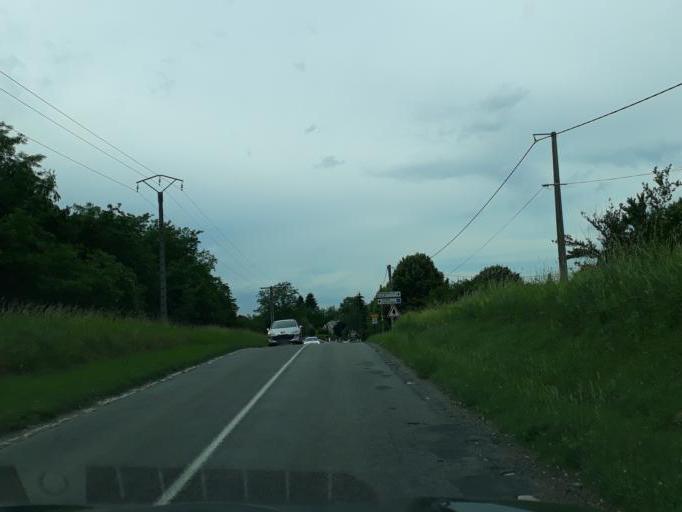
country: FR
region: Centre
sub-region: Departement du Loiret
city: Jargeau
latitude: 47.8549
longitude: 2.1305
